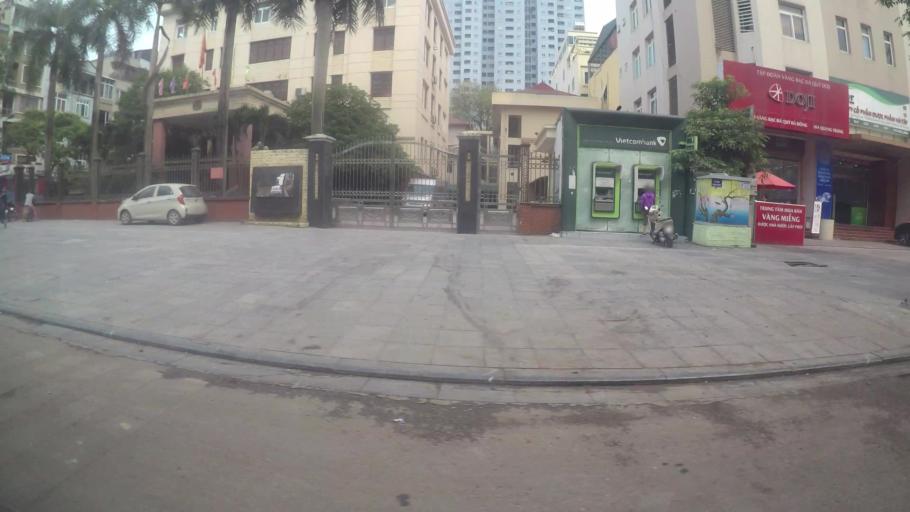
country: VN
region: Ha Noi
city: Ha Dong
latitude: 20.9720
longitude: 105.7767
